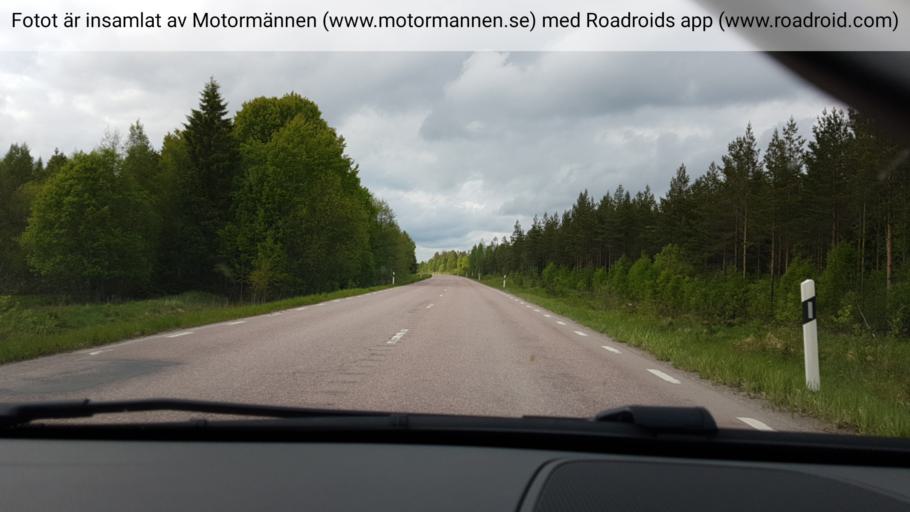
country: SE
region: Uppsala
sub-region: Tierps Kommun
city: Tierp
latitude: 60.2914
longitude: 17.5818
